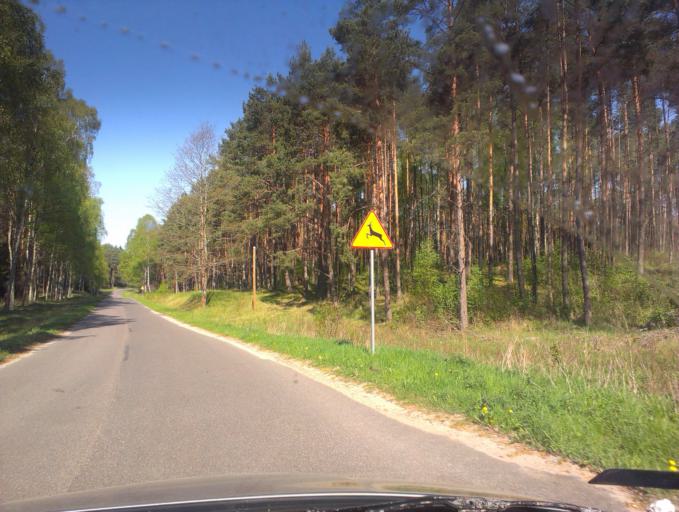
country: PL
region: West Pomeranian Voivodeship
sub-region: Powiat szczecinecki
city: Lubowo
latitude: 53.6329
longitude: 16.3422
